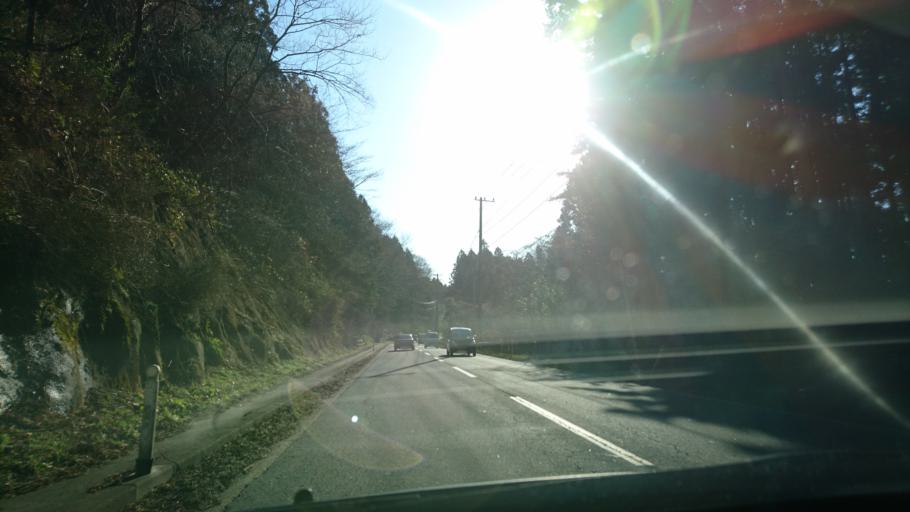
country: JP
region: Iwate
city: Ichinoseki
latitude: 38.9466
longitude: 141.1768
